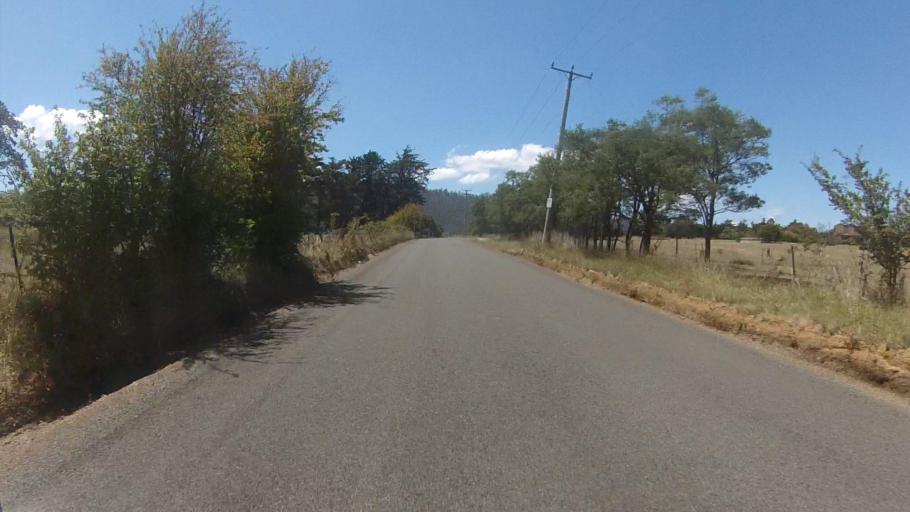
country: AU
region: Tasmania
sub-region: Sorell
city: Sorell
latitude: -42.7612
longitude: 147.6199
